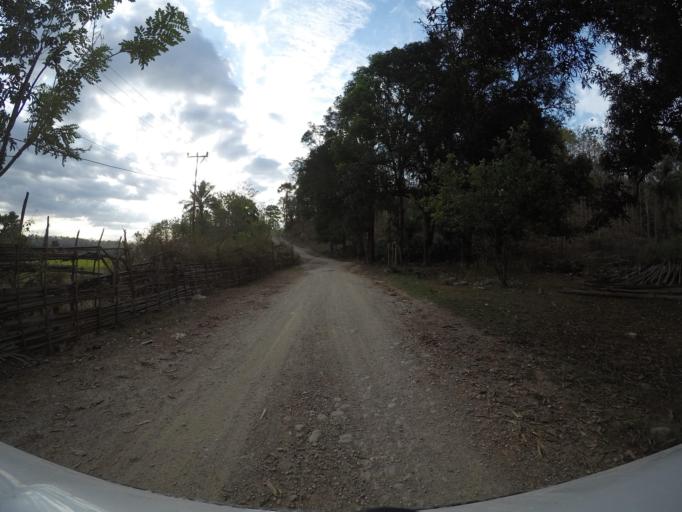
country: TL
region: Bobonaro
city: Maliana
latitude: -8.8929
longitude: 125.2114
